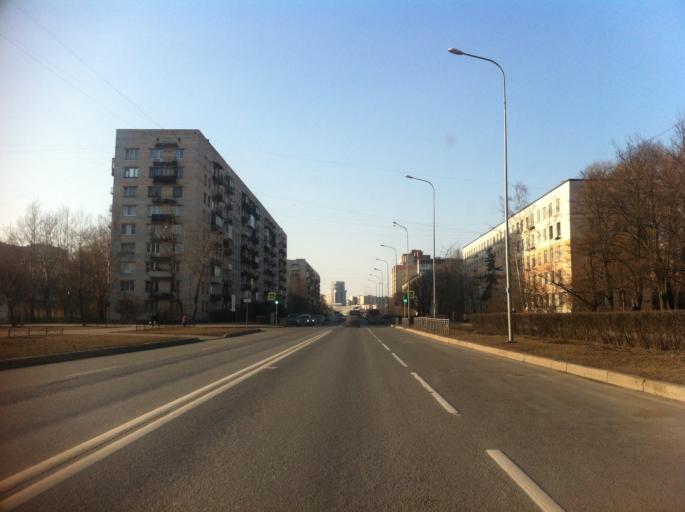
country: RU
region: St.-Petersburg
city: Dachnoye
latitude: 59.8439
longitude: 30.2332
